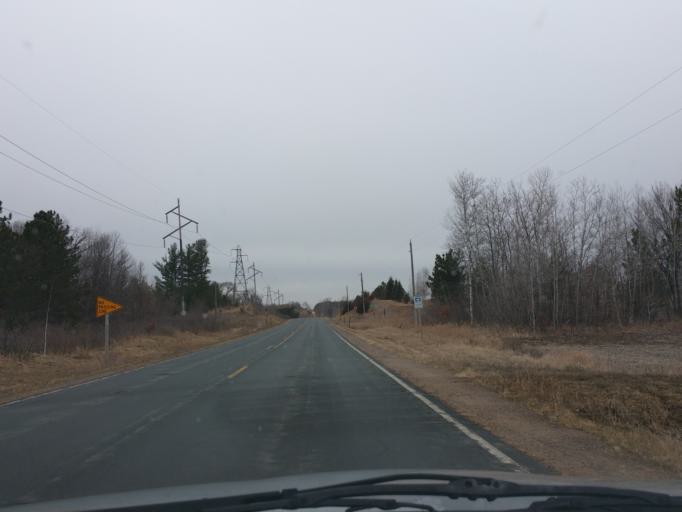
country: US
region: Wisconsin
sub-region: Saint Croix County
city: Roberts
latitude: 45.0357
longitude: -92.6260
